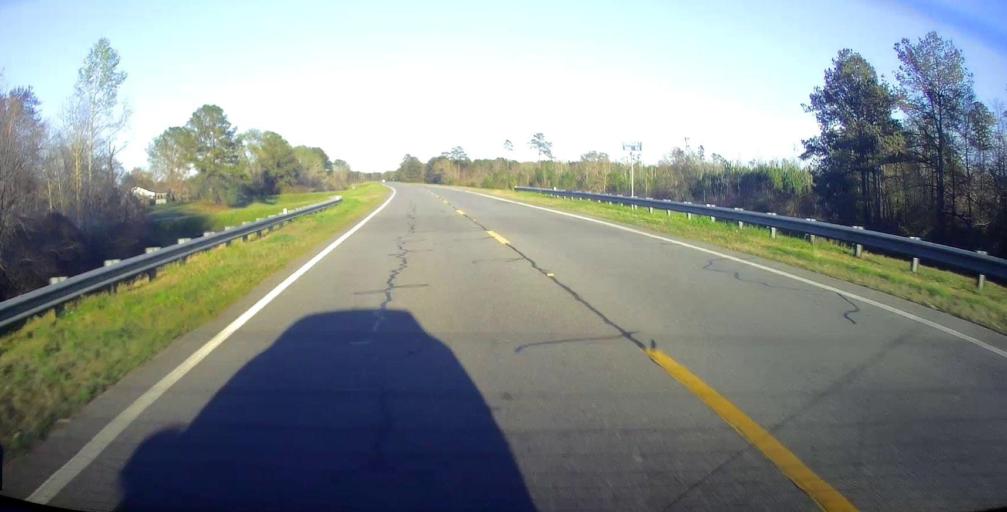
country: US
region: Georgia
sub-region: Wilcox County
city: Abbeville
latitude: 31.9986
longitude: -83.2674
